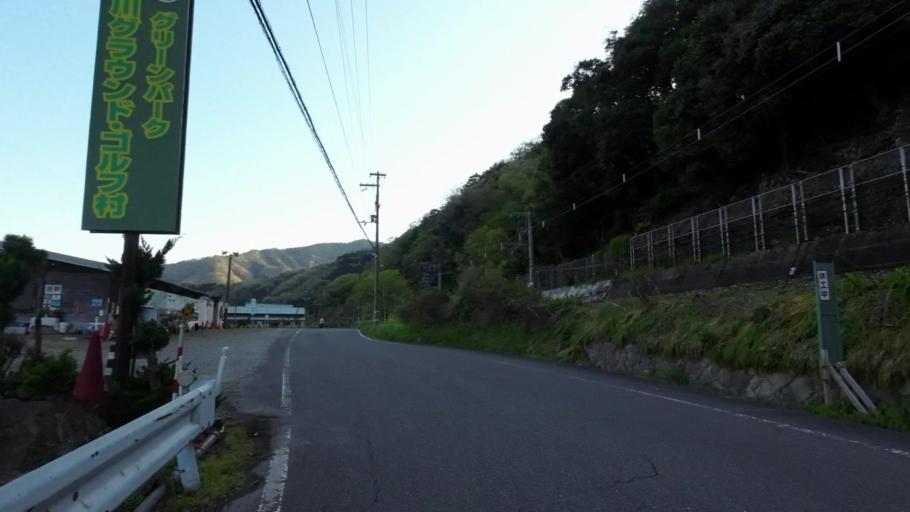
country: JP
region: Hyogo
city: Toyooka
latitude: 35.3781
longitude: 134.8110
